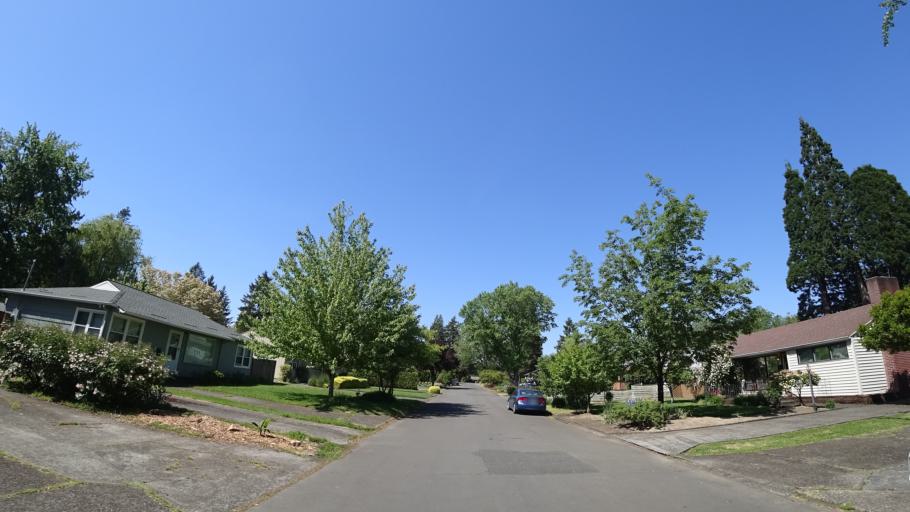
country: US
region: Oregon
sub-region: Washington County
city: Beaverton
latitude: 45.4946
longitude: -122.8033
